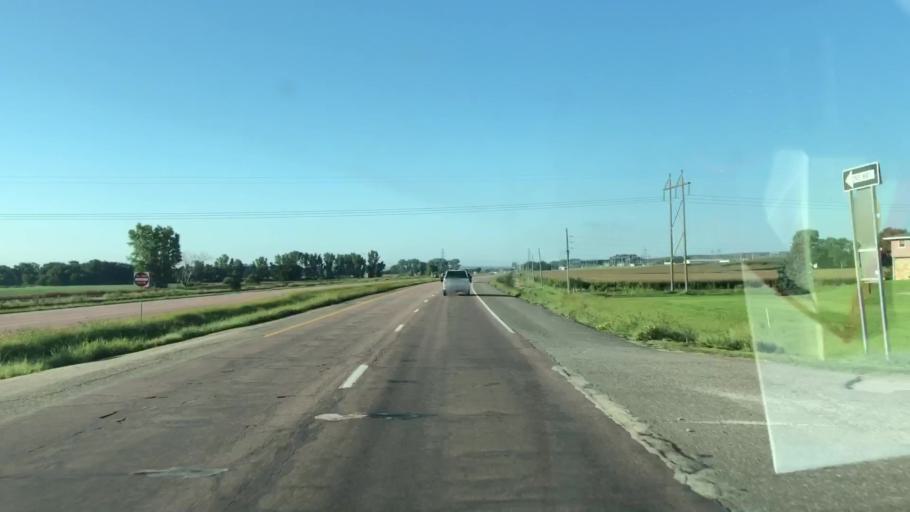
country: US
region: Iowa
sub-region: Woodbury County
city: Sioux City
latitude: 42.6130
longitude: -96.2962
